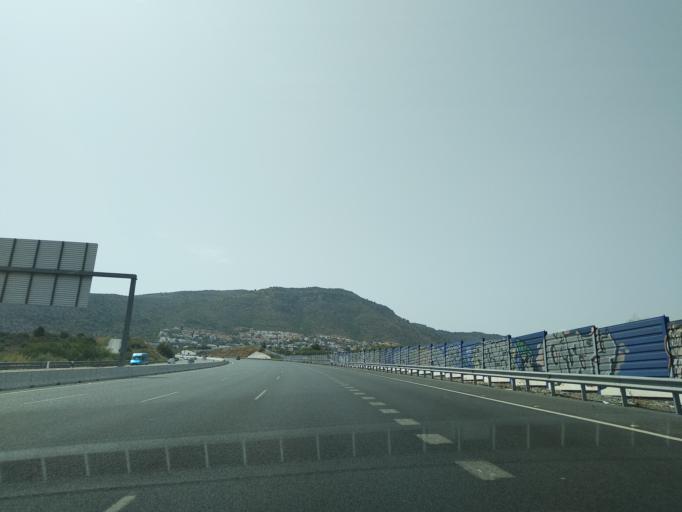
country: ES
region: Andalusia
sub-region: Provincia de Malaga
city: Alhaurin de la Torre
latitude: 36.6710
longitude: -4.5288
